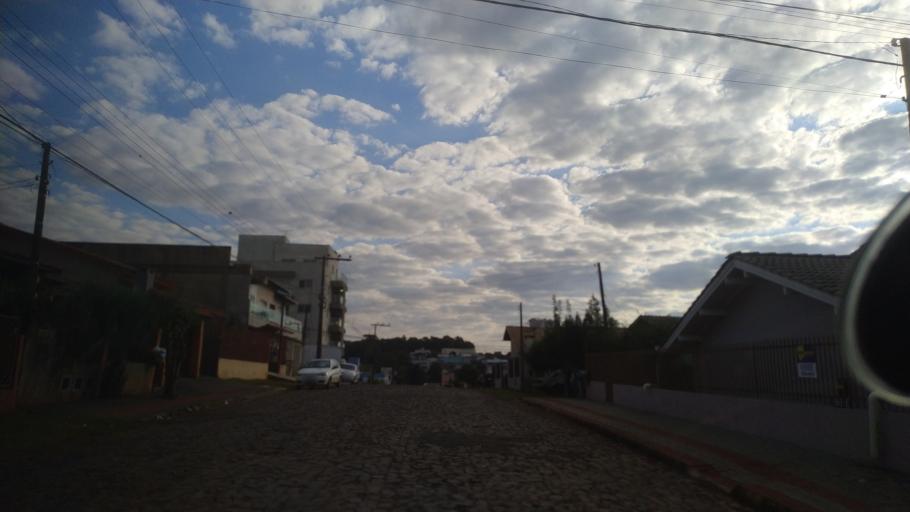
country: BR
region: Santa Catarina
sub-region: Chapeco
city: Chapeco
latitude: -27.0981
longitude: -52.6762
